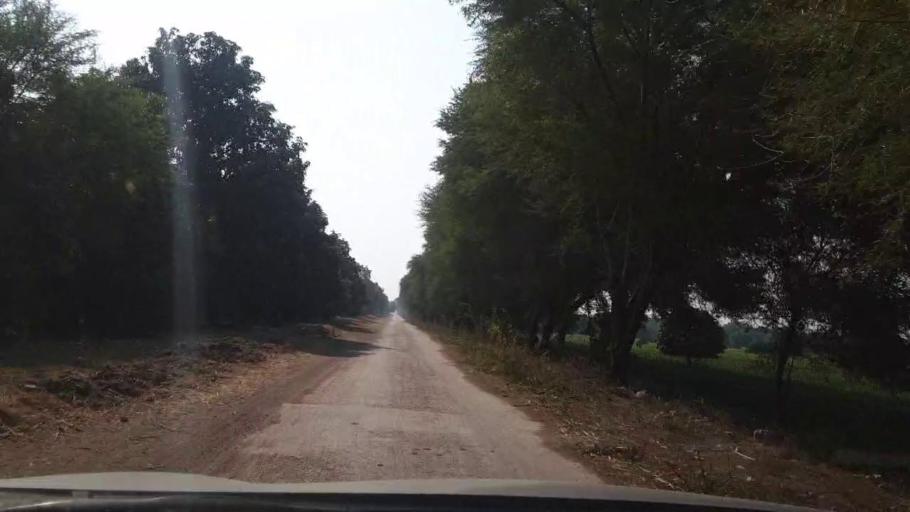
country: PK
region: Sindh
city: Tando Allahyar
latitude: 25.5135
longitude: 68.7861
